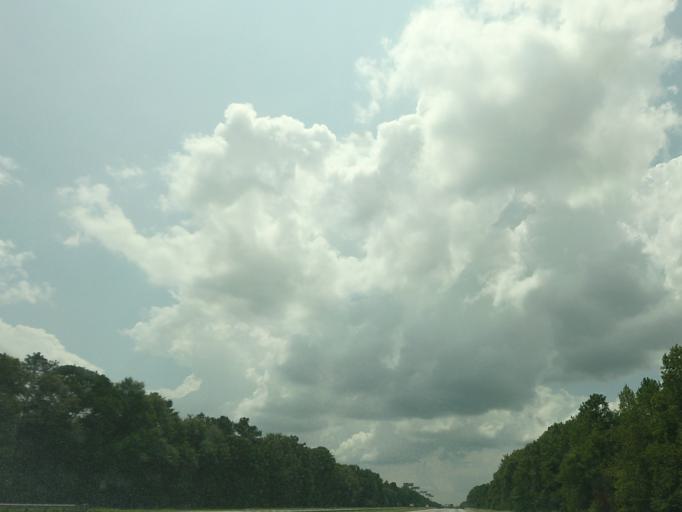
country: US
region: Georgia
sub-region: Peach County
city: Byron
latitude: 32.6421
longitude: -83.7439
